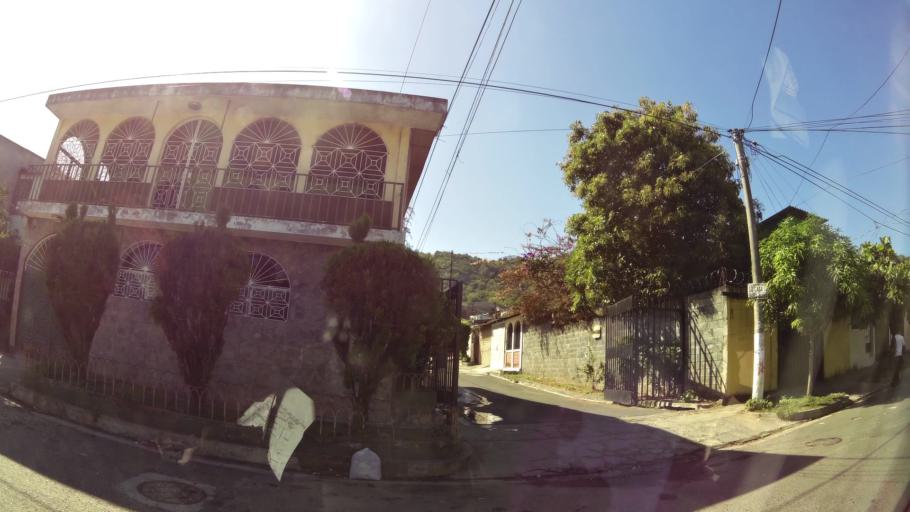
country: SV
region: La Libertad
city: Santa Tecla
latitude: 13.6676
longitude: -89.2861
